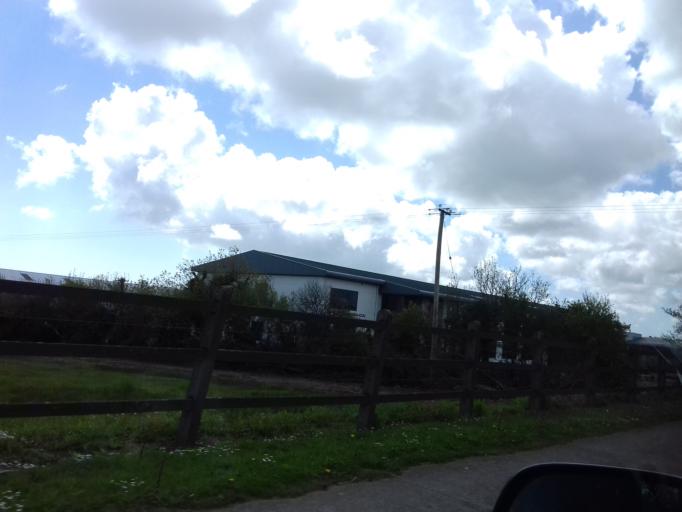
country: IE
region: Leinster
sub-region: Loch Garman
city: Castlebridge
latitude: 52.3606
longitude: -6.4523
